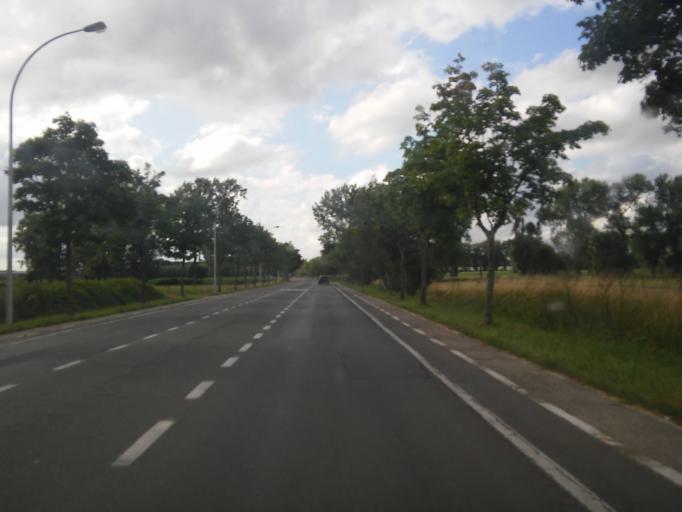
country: BE
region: Flanders
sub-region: Provincie Antwerpen
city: Aartselaar
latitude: 51.1446
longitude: 4.4083
